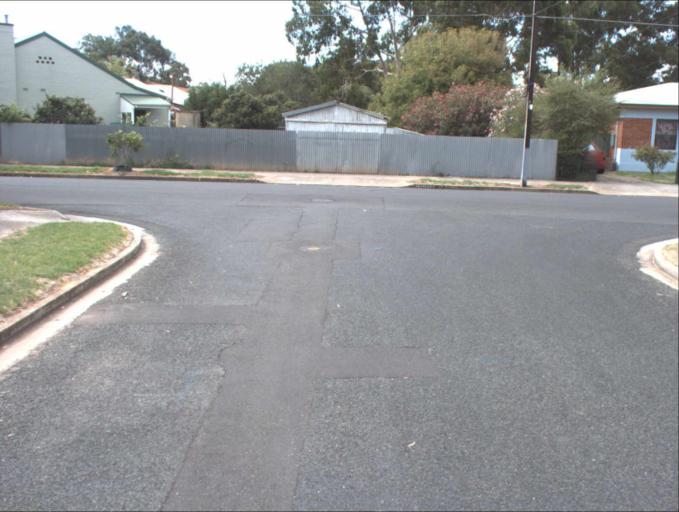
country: AU
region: South Australia
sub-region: Port Adelaide Enfield
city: Blair Athol
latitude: -34.8581
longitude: 138.5886
